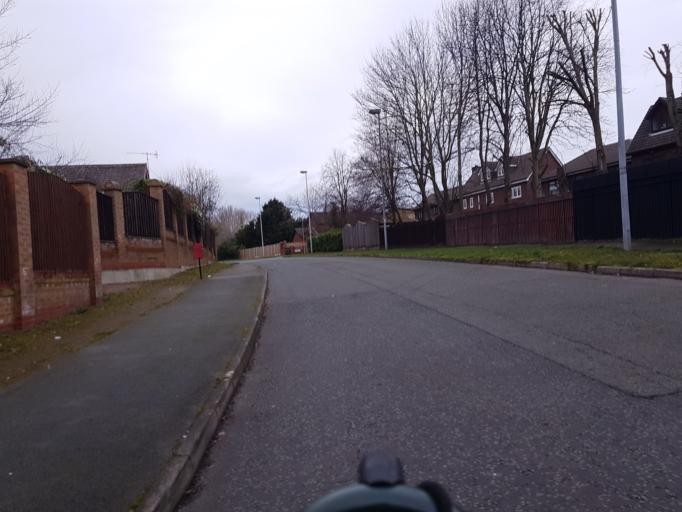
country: GB
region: England
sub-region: Metropolitan Borough of Wirral
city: Bromborough
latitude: 53.3761
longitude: -2.9600
